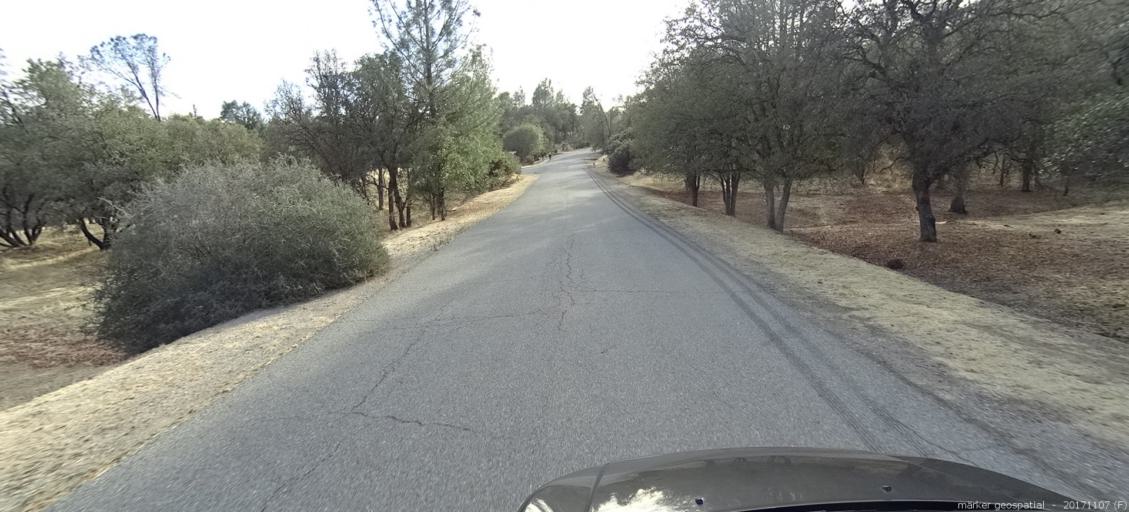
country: US
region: California
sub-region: Shasta County
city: Shasta
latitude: 40.5106
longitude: -122.4701
